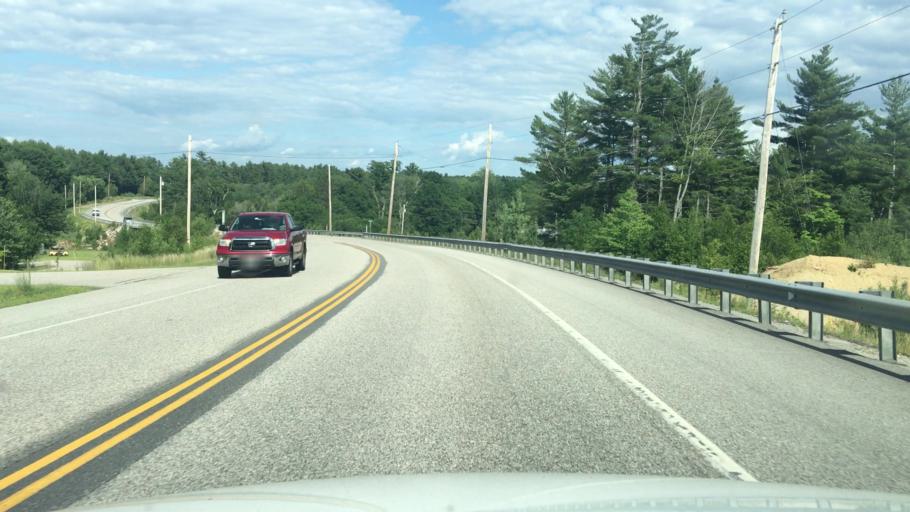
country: US
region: Maine
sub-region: Oxford County
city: Bethel
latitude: 44.3988
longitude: -70.8772
